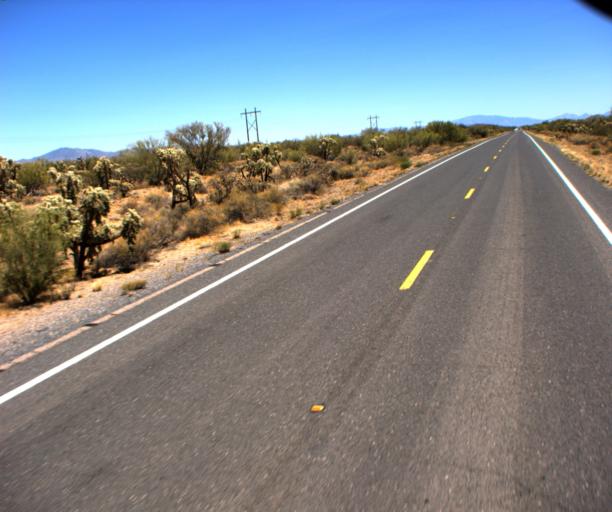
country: US
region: Arizona
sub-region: Pinal County
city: Florence
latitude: 32.8129
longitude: -111.1948
